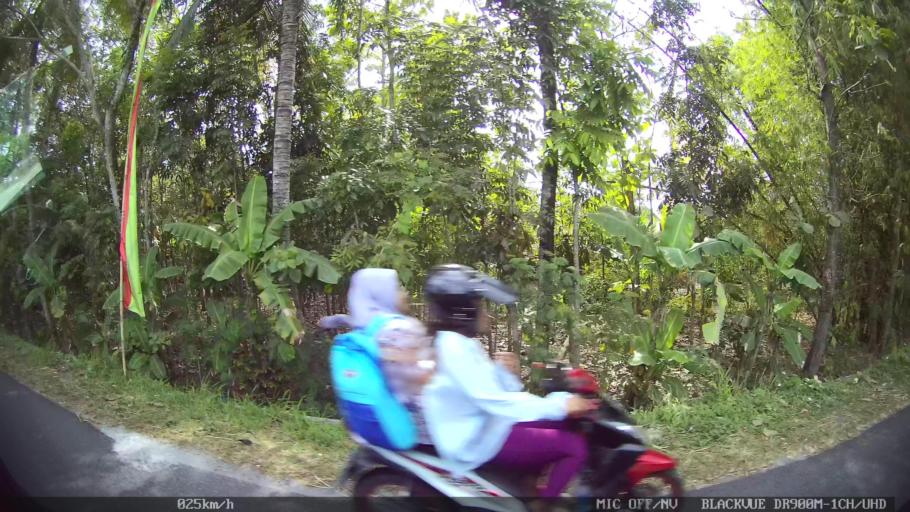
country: ID
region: Daerah Istimewa Yogyakarta
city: Kasihan
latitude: -7.8499
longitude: 110.3144
